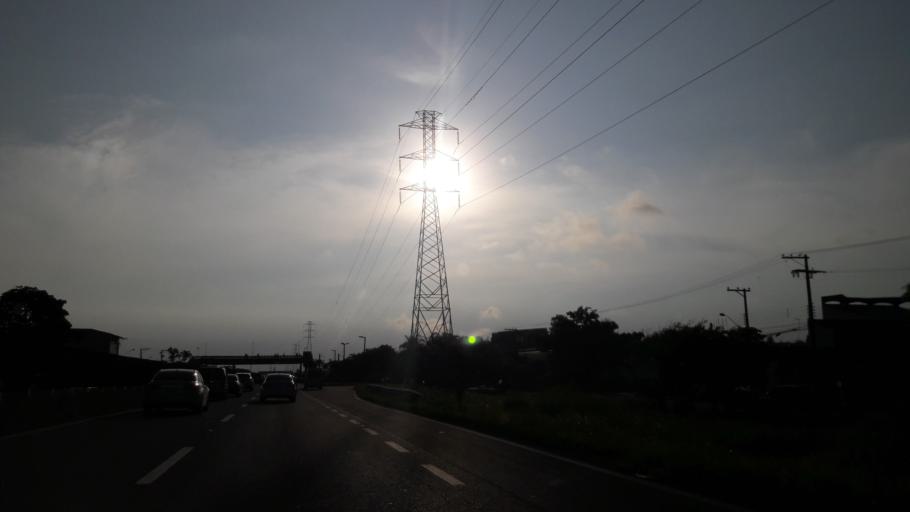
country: BR
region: Sao Paulo
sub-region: Itanhaem
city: Itanhaem
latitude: -24.1596
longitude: -46.7513
